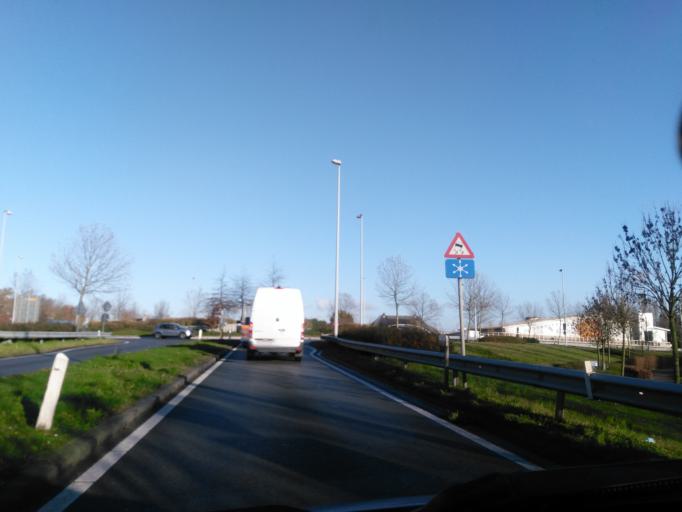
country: BE
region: Flanders
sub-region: Provincie Antwerpen
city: Zwijndrecht
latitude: 51.2182
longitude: 4.3078
